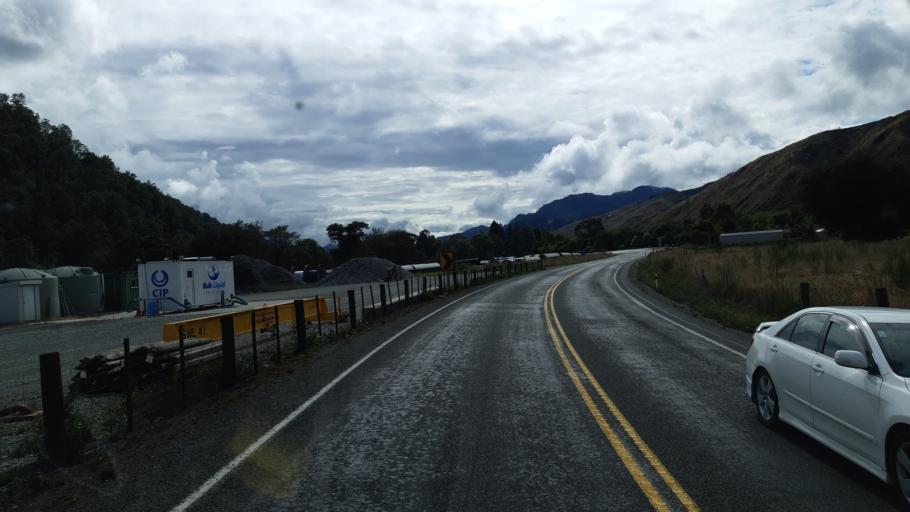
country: NZ
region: West Coast
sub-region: Buller District
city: Westport
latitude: -41.7911
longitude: 172.3655
